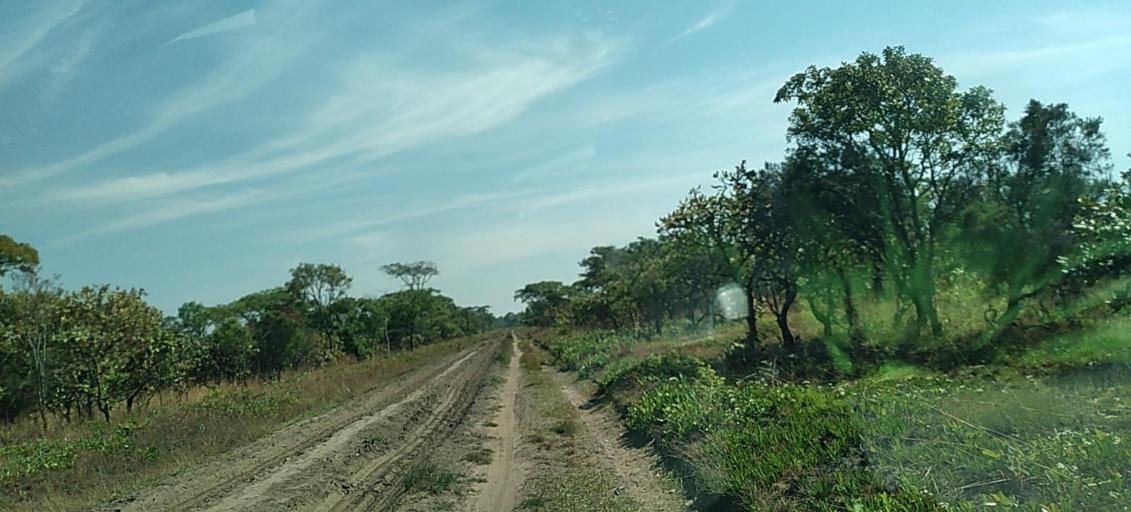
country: ZM
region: North-Western
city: Mwinilunga
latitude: -11.8035
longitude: 25.1655
